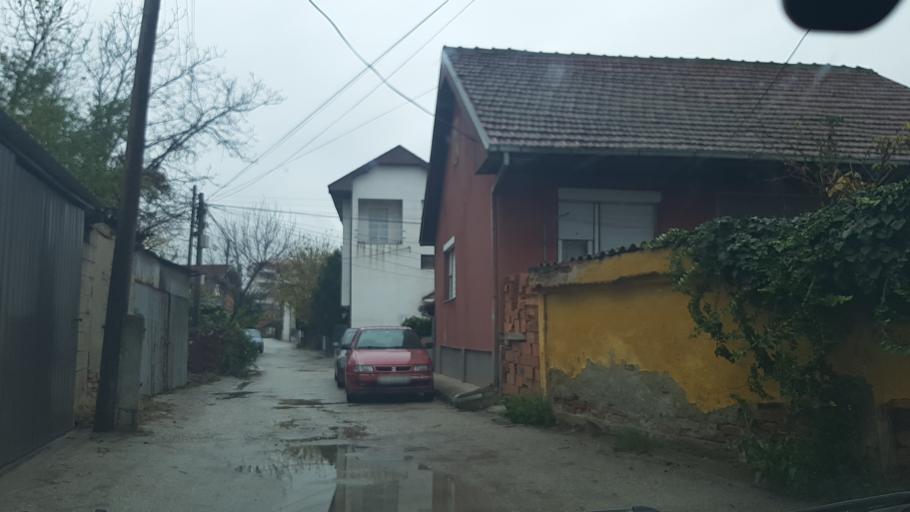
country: MK
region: Karpos
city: Skopje
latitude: 41.9951
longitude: 21.4469
